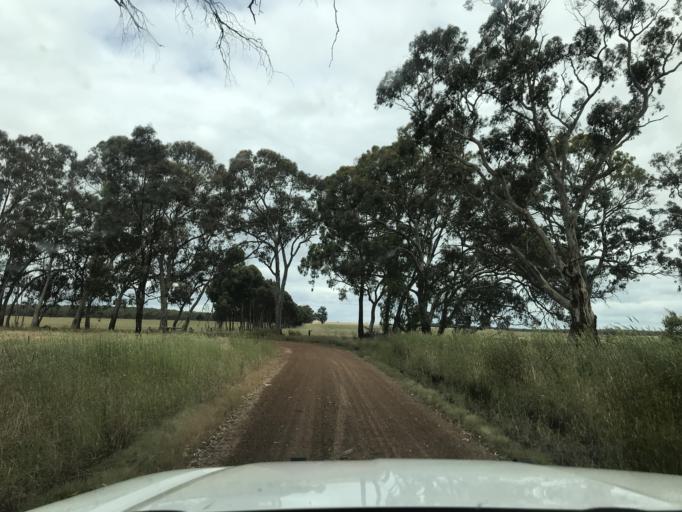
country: AU
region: South Australia
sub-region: Naracoorte and Lucindale
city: Naracoorte
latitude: -36.9257
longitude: 141.3152
